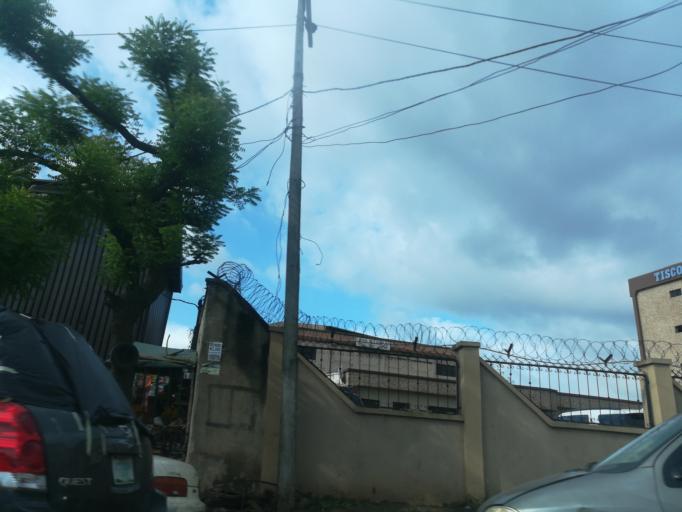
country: NG
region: Lagos
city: Ikeja
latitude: 6.6206
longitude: 3.3556
